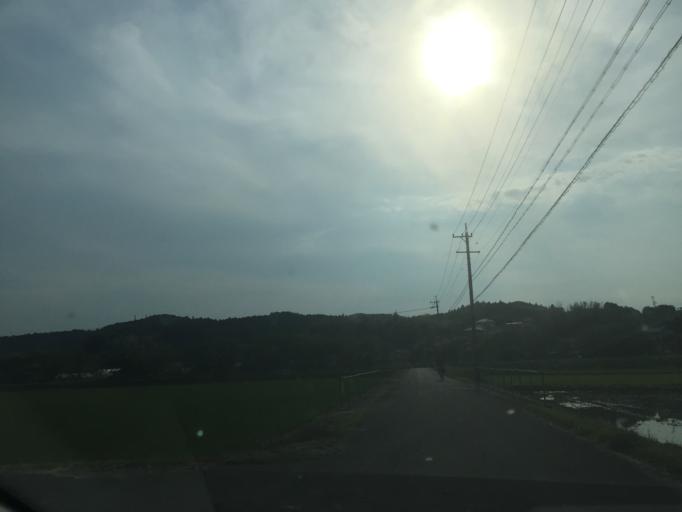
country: JP
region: Shizuoka
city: Mori
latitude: 34.8249
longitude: 137.9589
